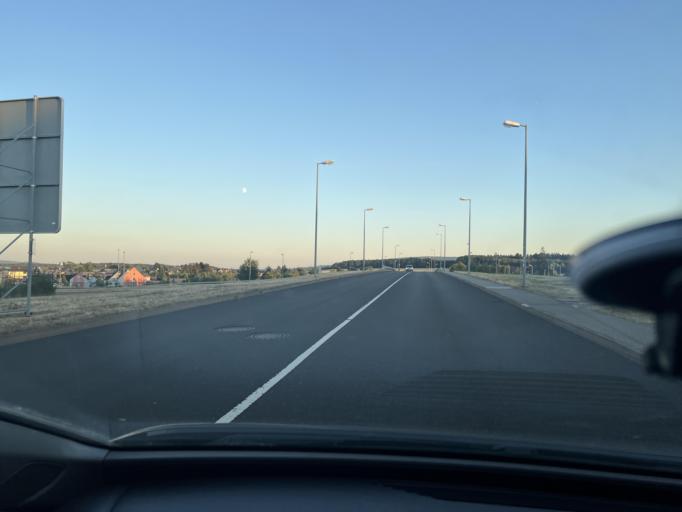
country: DE
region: Rheinland-Pfalz
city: Lautzenhausen
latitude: 49.9419
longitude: 7.2668
